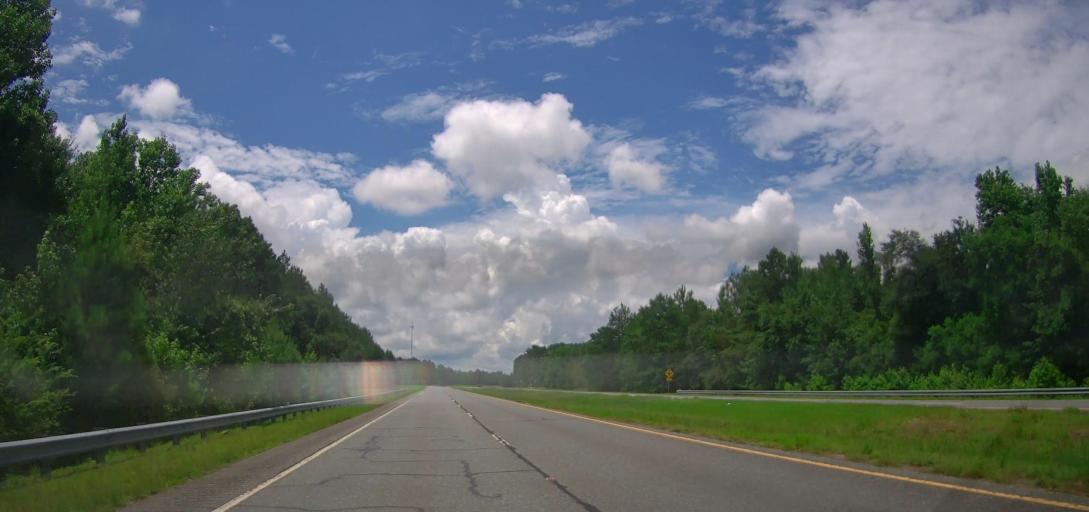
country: US
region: Georgia
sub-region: Dodge County
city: Eastman
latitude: 32.1841
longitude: -83.1973
